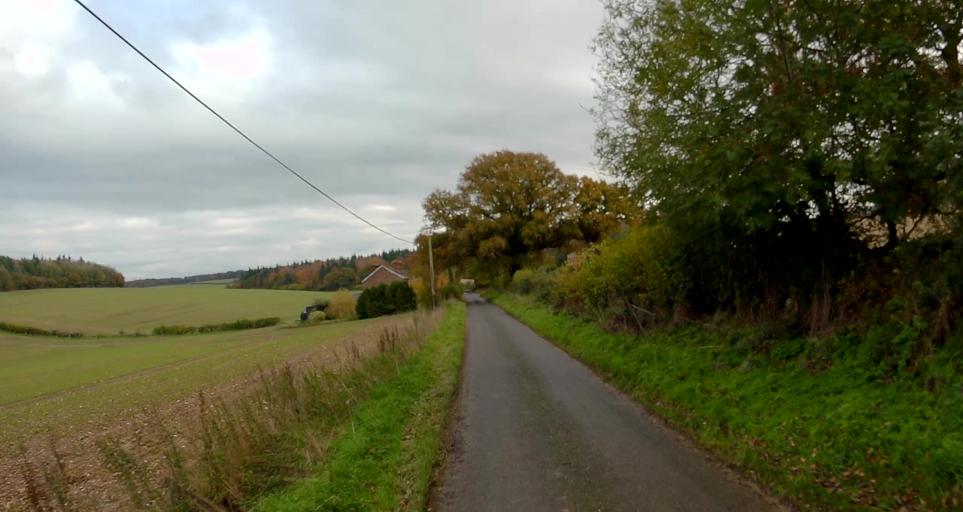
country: GB
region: England
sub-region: Hampshire
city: Long Sutton
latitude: 51.2112
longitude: -0.9570
